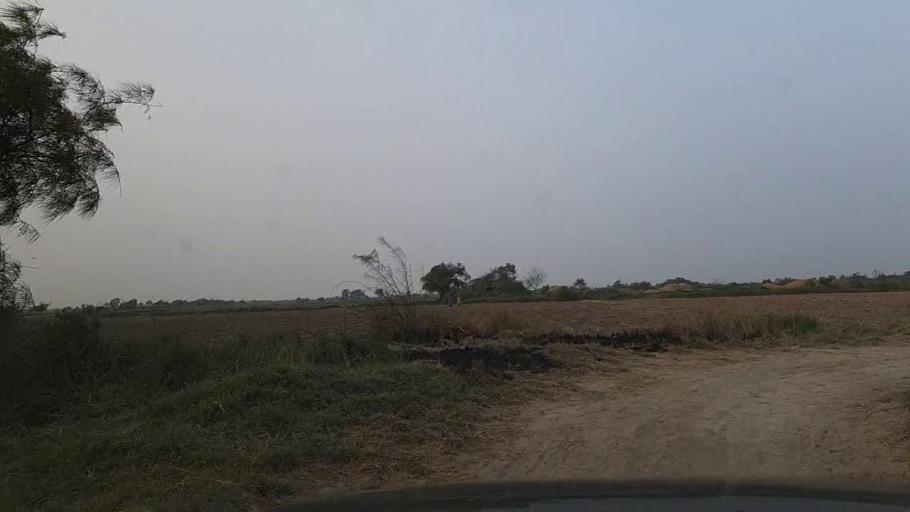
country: PK
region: Sindh
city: Gharo
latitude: 24.7379
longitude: 67.7057
